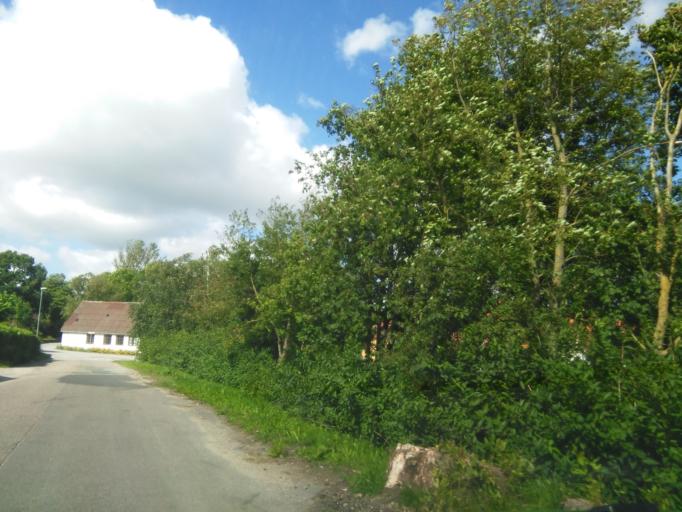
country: DK
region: Central Jutland
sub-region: Syddjurs Kommune
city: Ronde
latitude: 56.1840
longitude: 10.4865
